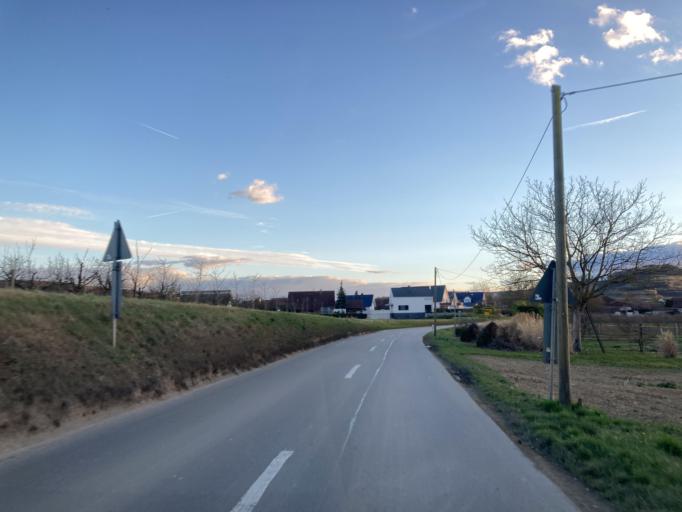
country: DE
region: Baden-Wuerttemberg
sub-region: Freiburg Region
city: Sasbach
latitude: 48.1248
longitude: 7.6083
